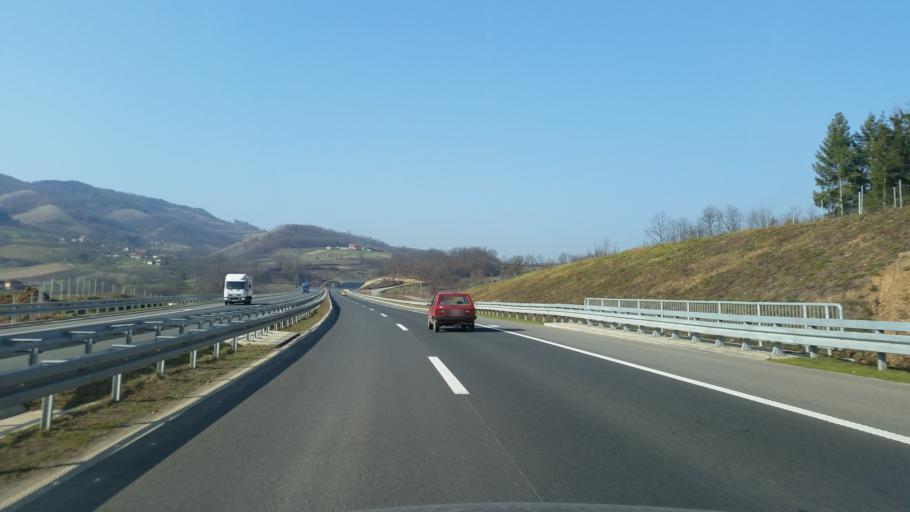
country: RS
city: Prislonica
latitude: 44.0008
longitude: 20.4009
